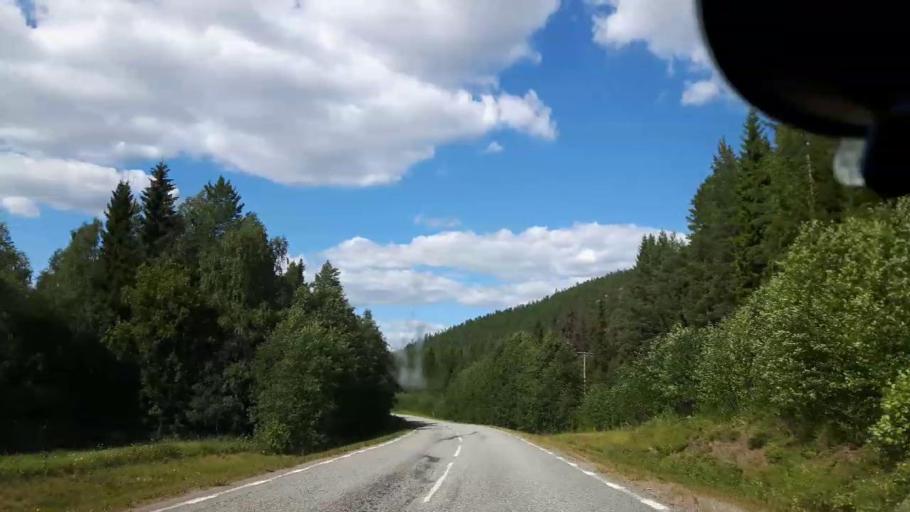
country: SE
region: Vaesternorrland
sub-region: Ange Kommun
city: Fransta
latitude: 62.7390
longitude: 16.3320
